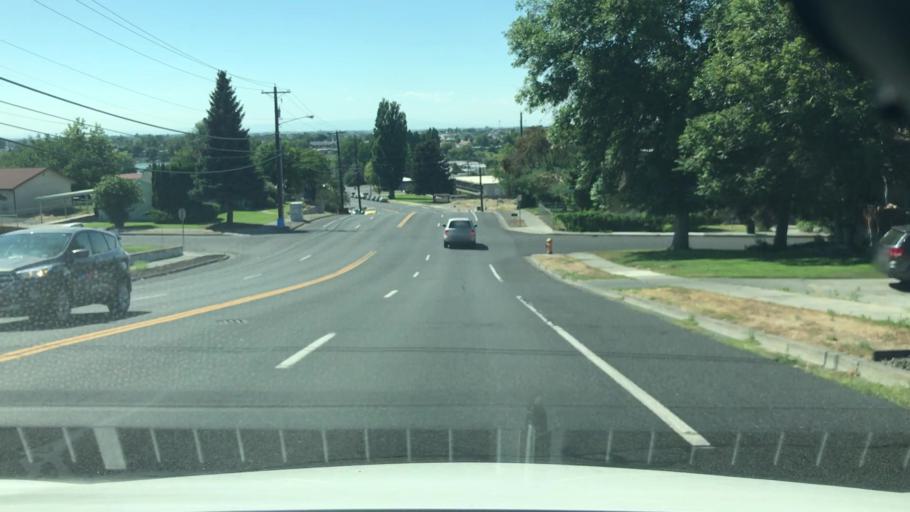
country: US
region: Washington
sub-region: Grant County
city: Moses Lake
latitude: 47.1212
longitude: -119.2705
